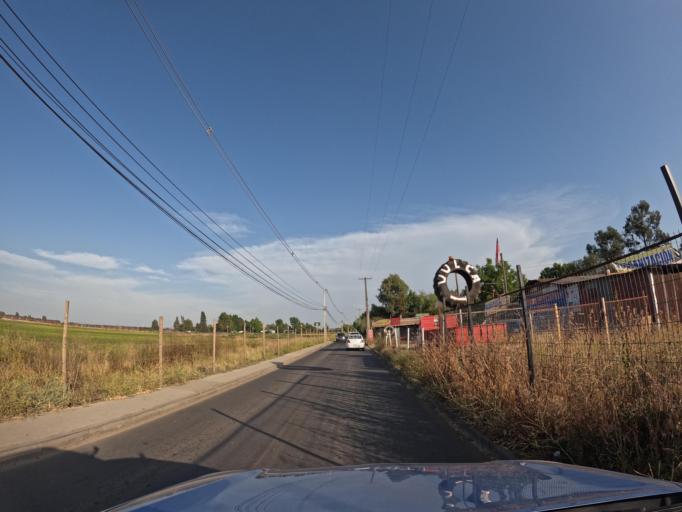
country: CL
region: Maule
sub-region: Provincia de Talca
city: Talca
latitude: -35.4469
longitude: -71.6210
